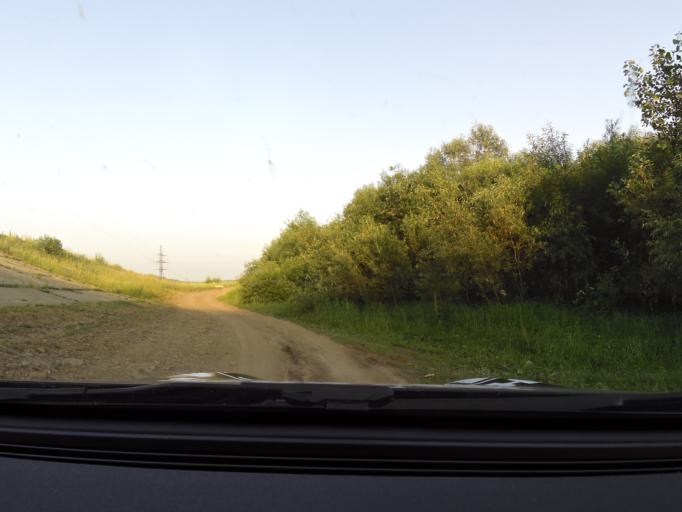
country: RU
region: Sverdlovsk
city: Mikhaylovsk
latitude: 56.4248
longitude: 59.0656
